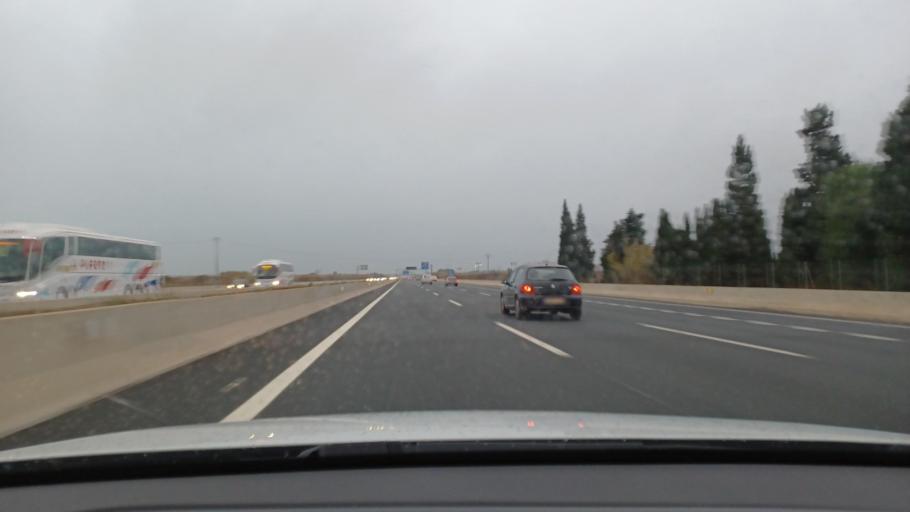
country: ES
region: Valencia
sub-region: Provincia de Valencia
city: Albuixech
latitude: 39.5611
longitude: -0.2965
